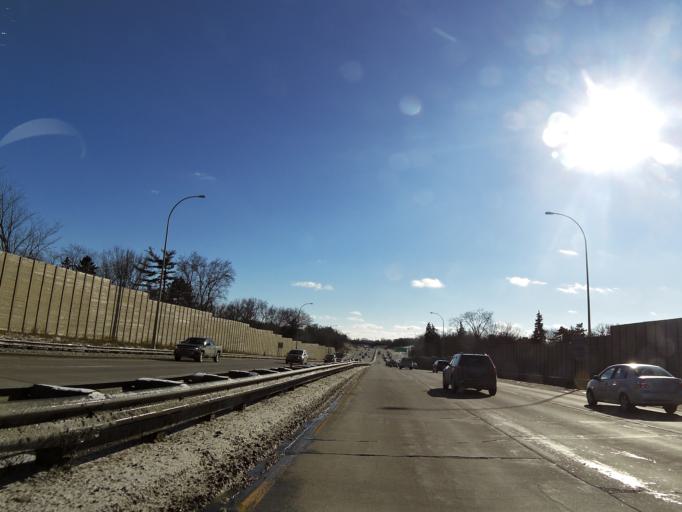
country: US
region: Minnesota
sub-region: Hennepin County
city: Edina
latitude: 44.9187
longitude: -93.3499
